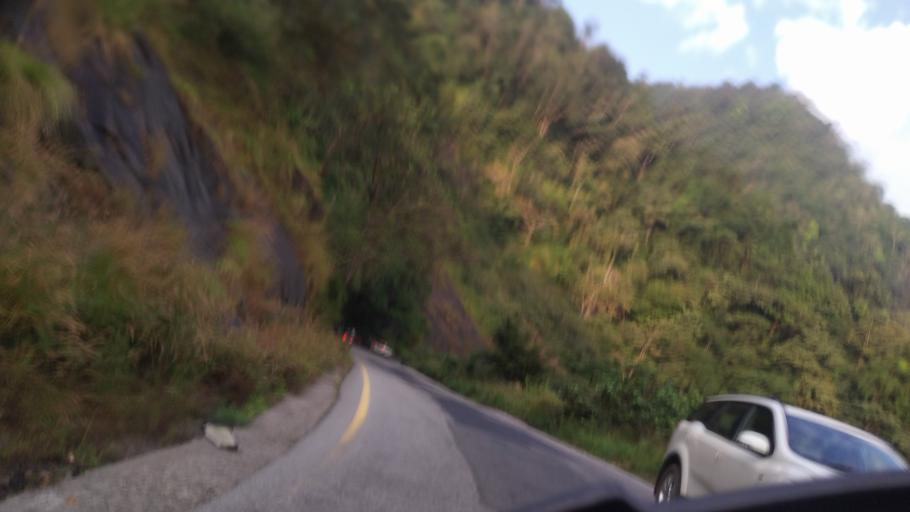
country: IN
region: Kerala
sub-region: Wayanad
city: Kalpetta
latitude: 11.5107
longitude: 76.0196
